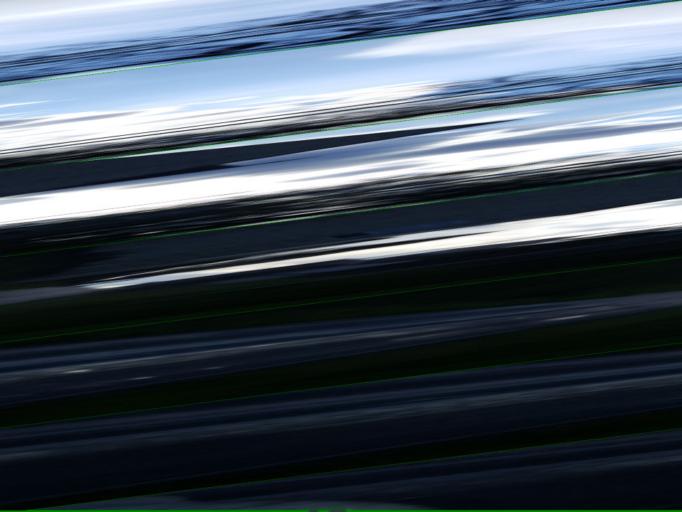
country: FR
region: Ile-de-France
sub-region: Departement du Val-d'Oise
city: Magny-en-Vexin
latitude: 49.1869
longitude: 1.8551
